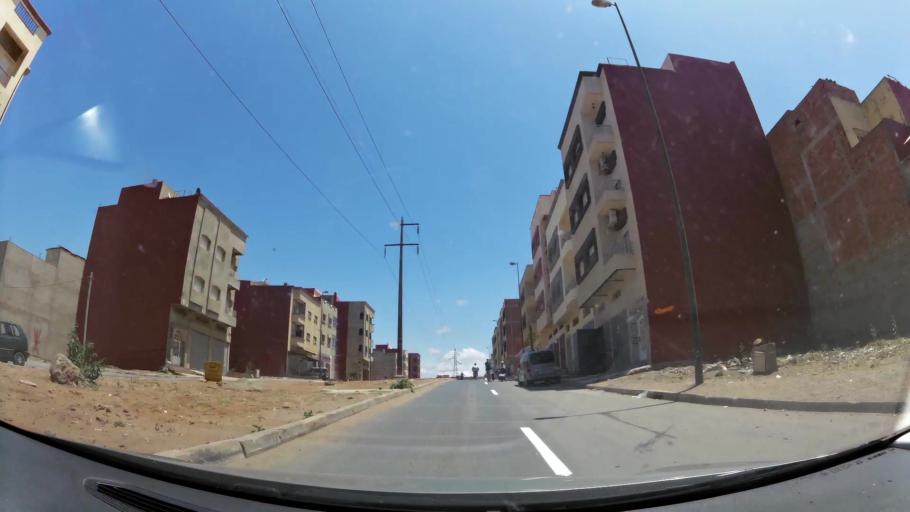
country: MA
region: Gharb-Chrarda-Beni Hssen
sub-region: Kenitra Province
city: Kenitra
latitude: 34.2352
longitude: -6.6186
